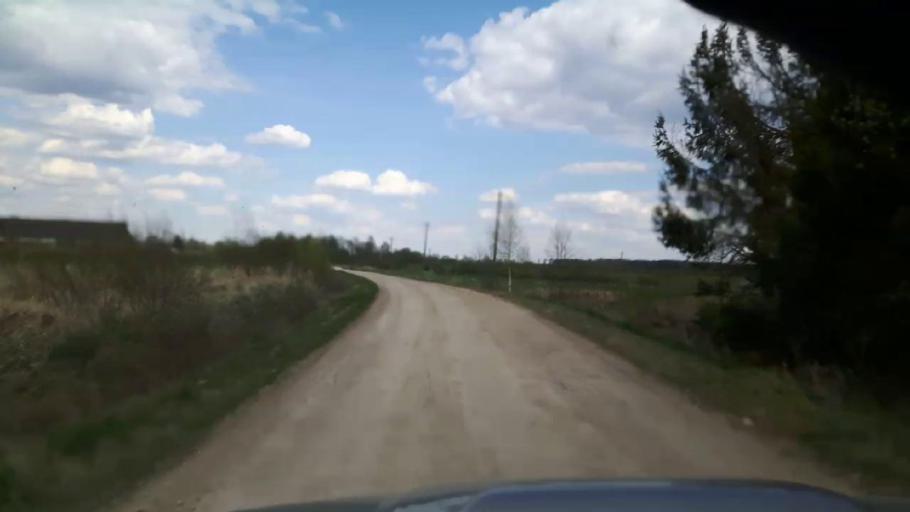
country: EE
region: Paernumaa
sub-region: Sindi linn
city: Sindi
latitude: 58.4106
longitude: 24.6967
